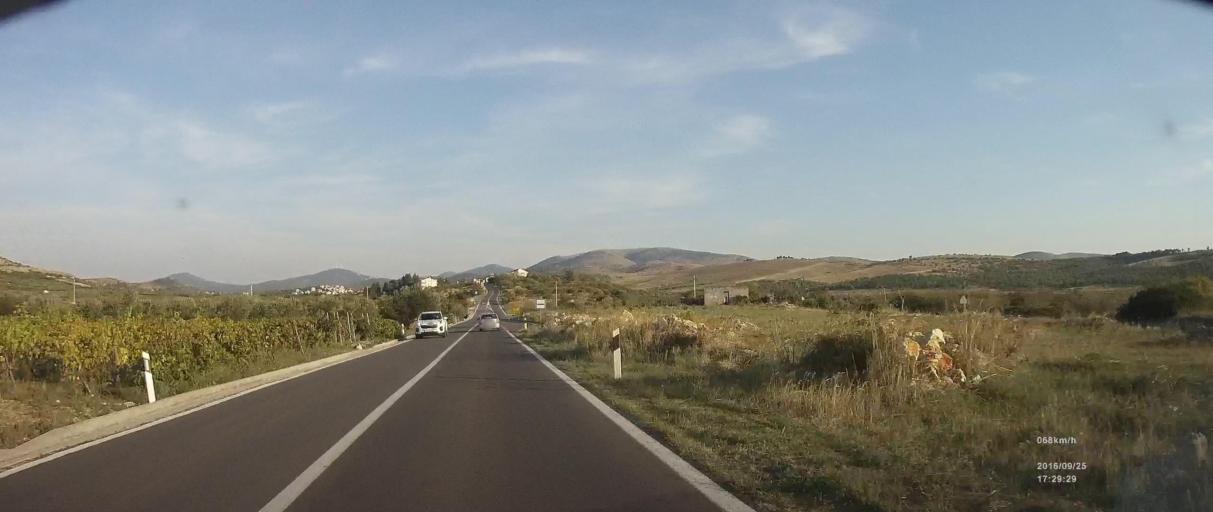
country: HR
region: Sibensko-Kniniska
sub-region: Grad Sibenik
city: Brodarica
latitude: 43.6860
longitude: 15.9660
